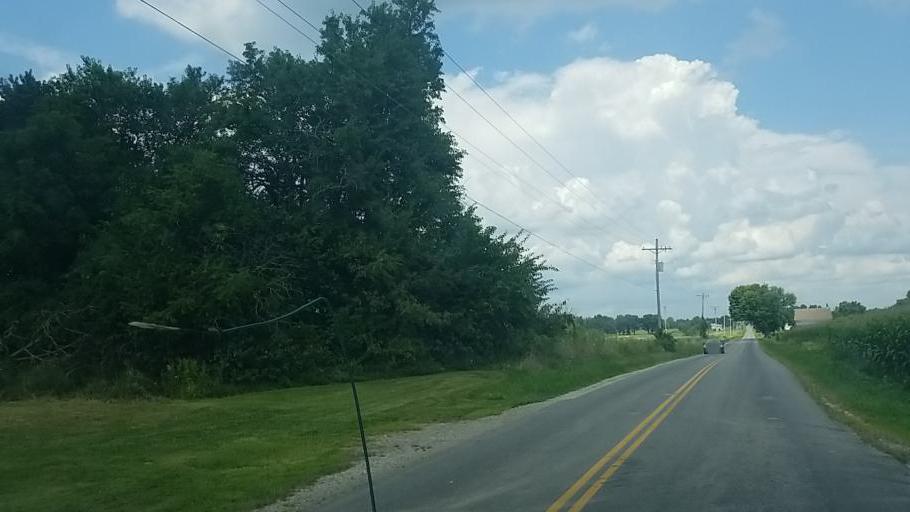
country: US
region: Ohio
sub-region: Medina County
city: Lodi
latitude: 41.0538
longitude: -82.0768
